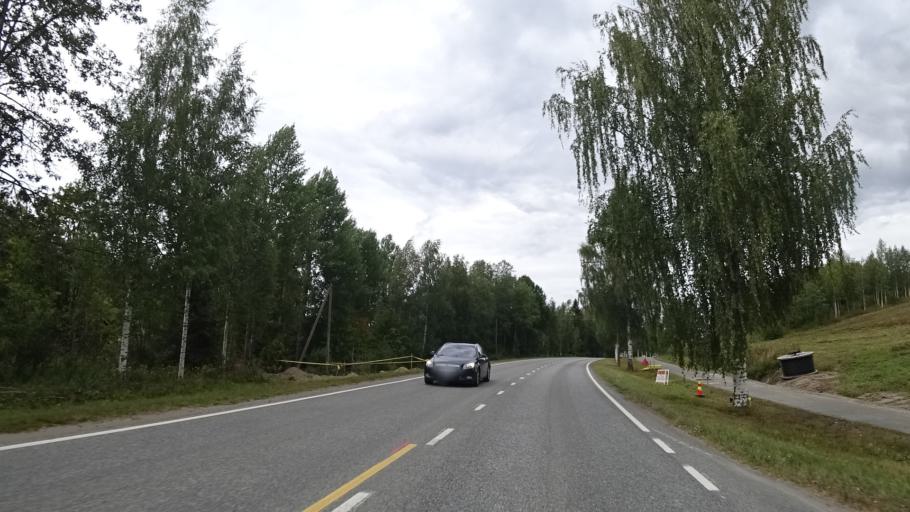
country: FI
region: North Karelia
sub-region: Joensuu
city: Ilomantsi
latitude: 62.6584
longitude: 30.9331
